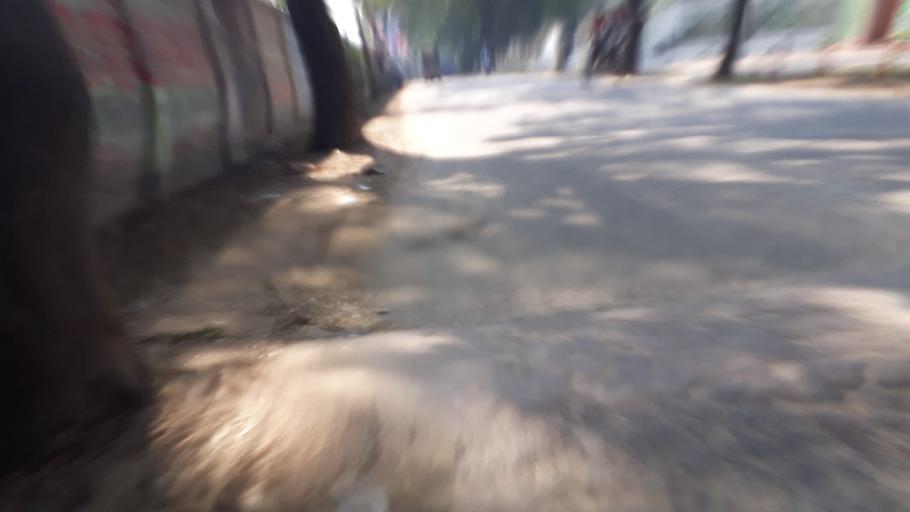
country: BD
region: Dhaka
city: Tungi
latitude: 23.9005
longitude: 90.2758
